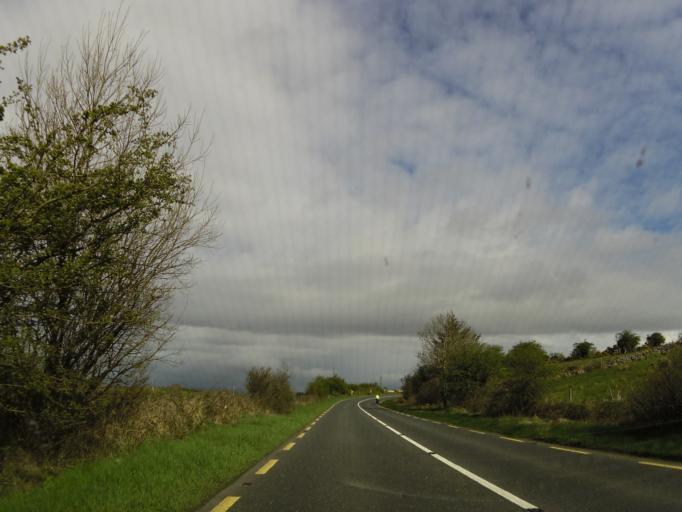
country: IE
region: Connaught
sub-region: Sligo
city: Tobercurry
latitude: 53.9466
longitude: -8.7930
